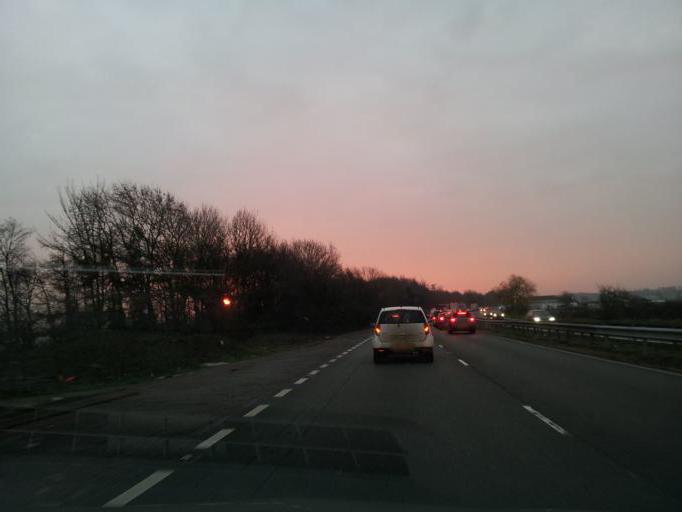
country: GB
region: England
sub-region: Peterborough
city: Thornhaugh
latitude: 52.6005
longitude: -0.4228
